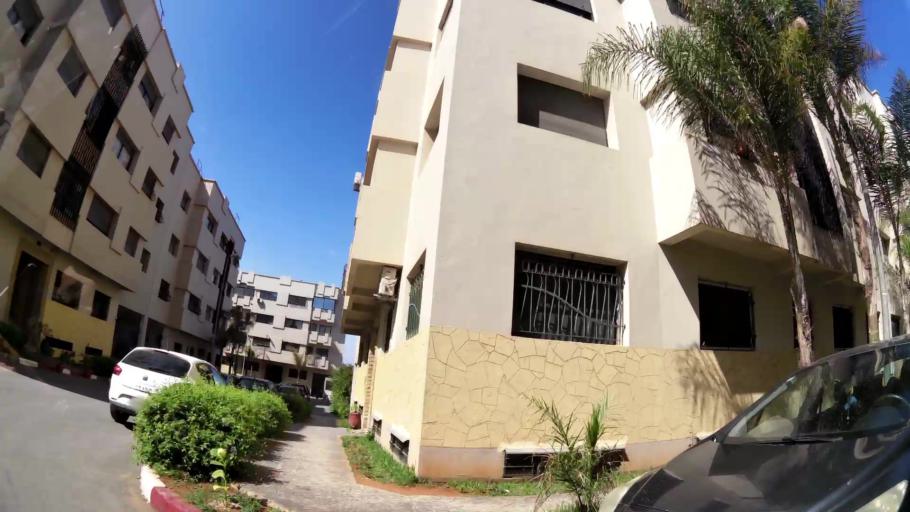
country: MA
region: Rabat-Sale-Zemmour-Zaer
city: Sale
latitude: 34.0646
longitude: -6.8014
